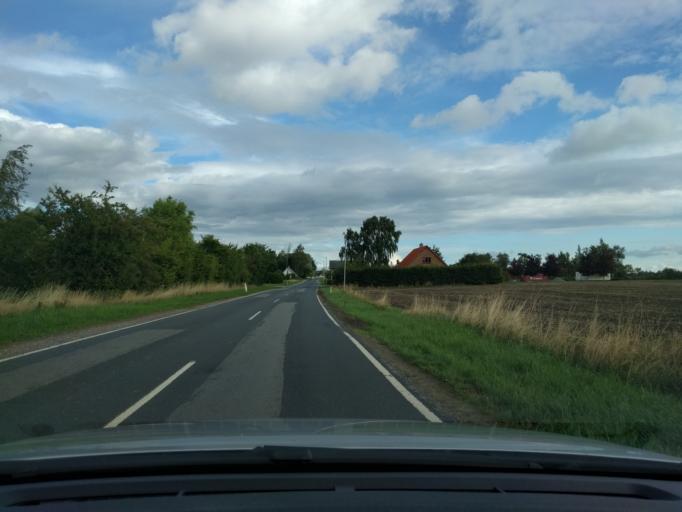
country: DK
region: South Denmark
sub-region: Nyborg Kommune
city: Ullerslev
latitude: 55.3944
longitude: 10.6657
